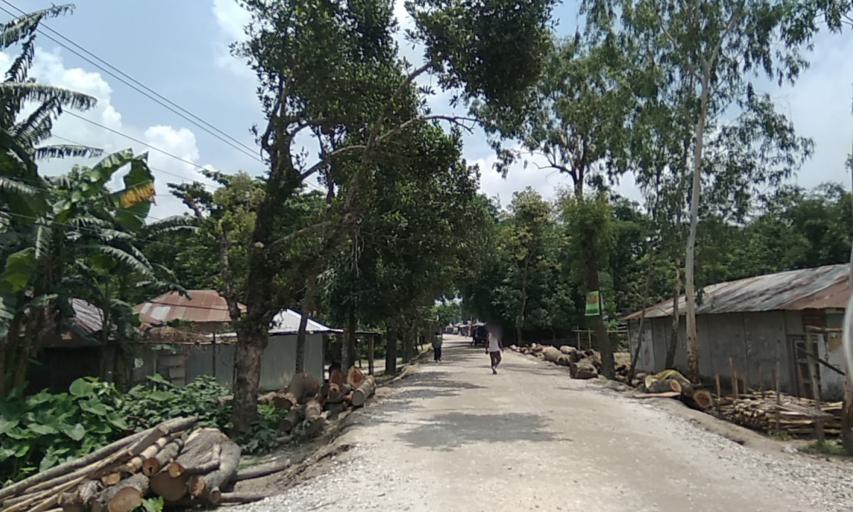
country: BD
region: Rangpur Division
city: Rangpur
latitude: 25.8877
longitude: 89.1850
